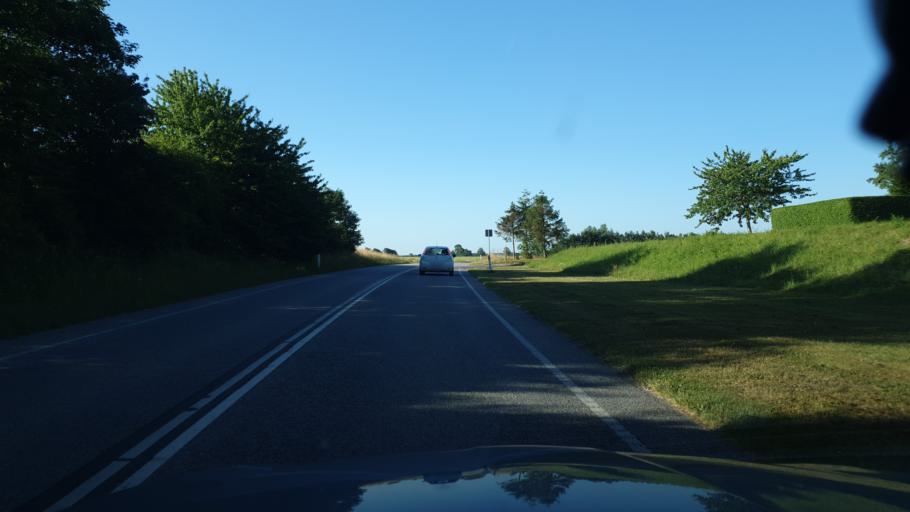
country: DK
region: Zealand
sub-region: Soro Kommune
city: Frederiksberg
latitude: 55.3829
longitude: 11.6511
